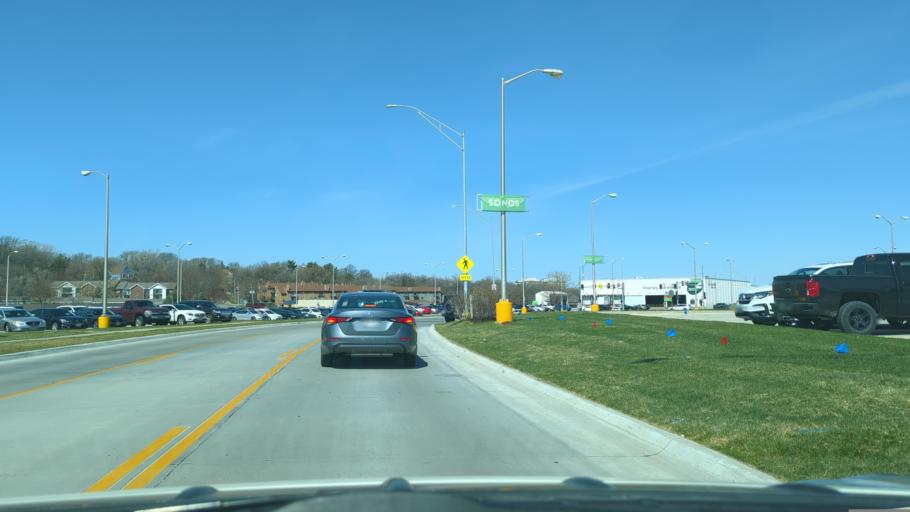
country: US
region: Nebraska
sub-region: Douglas County
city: Ralston
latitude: 41.2520
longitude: -96.0264
